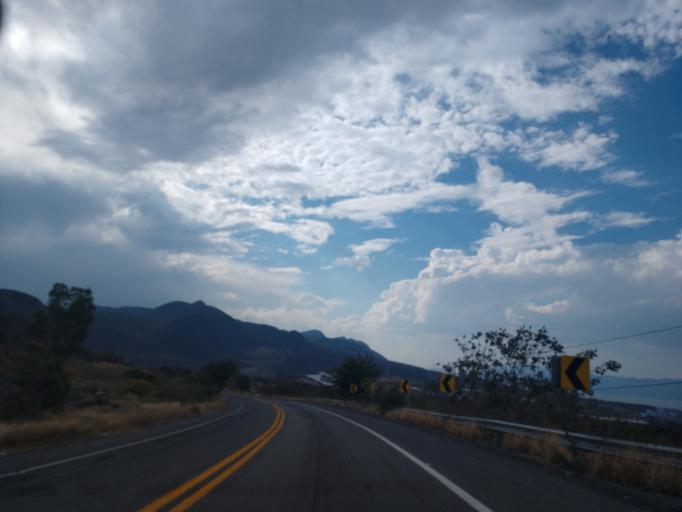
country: MX
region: Jalisco
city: Tizapan el Alto
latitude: 20.1348
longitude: -103.1713
